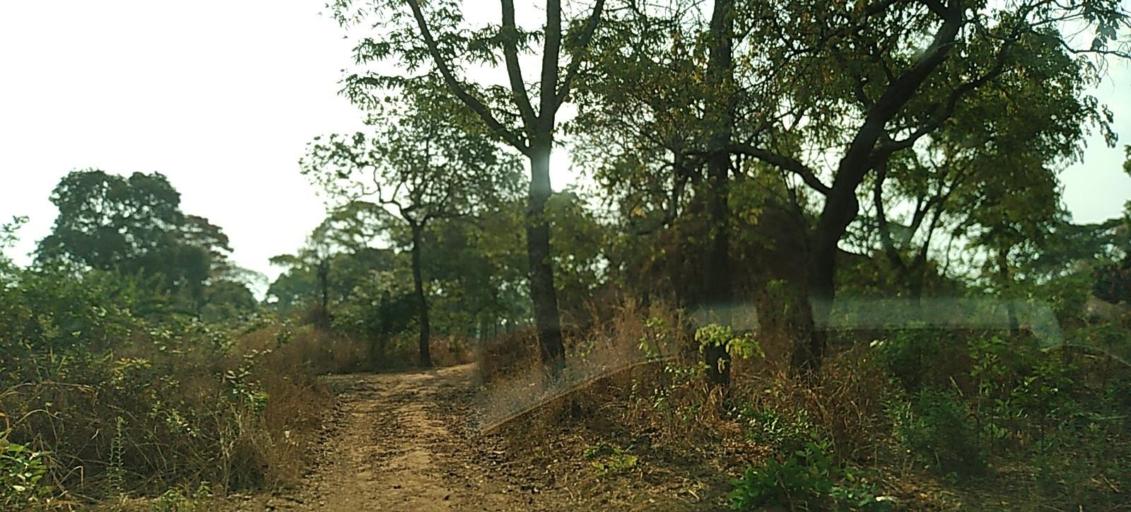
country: ZM
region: North-Western
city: Solwezi
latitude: -12.0548
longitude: 26.1495
